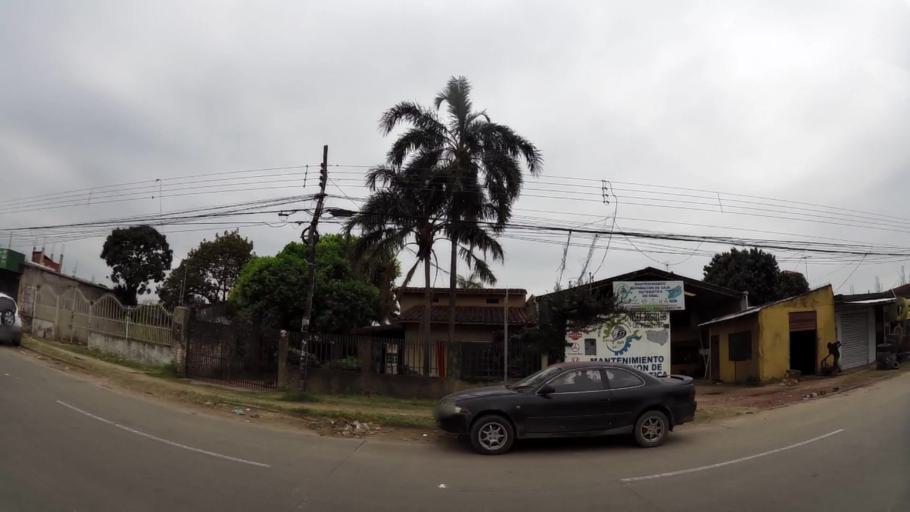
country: BO
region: Santa Cruz
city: Santa Cruz de la Sierra
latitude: -17.8326
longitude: -63.1844
